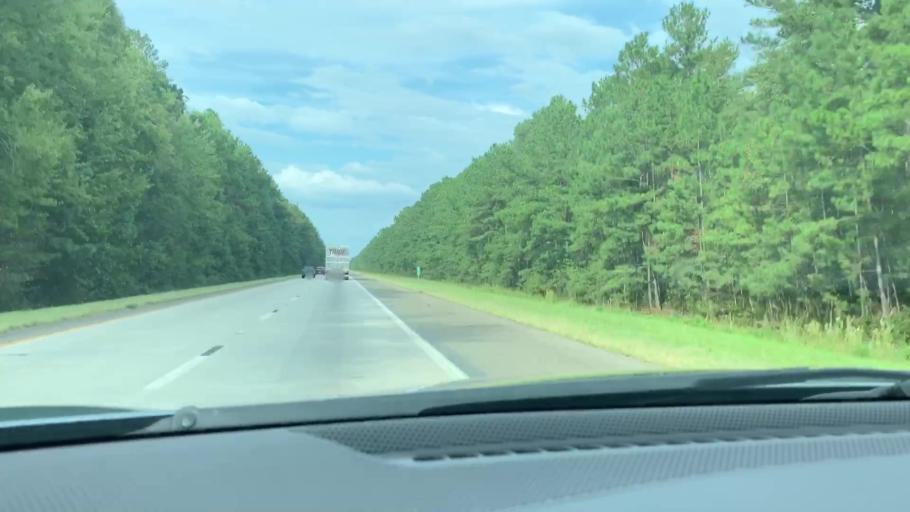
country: US
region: South Carolina
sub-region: Colleton County
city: Walterboro
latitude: 33.0515
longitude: -80.6671
